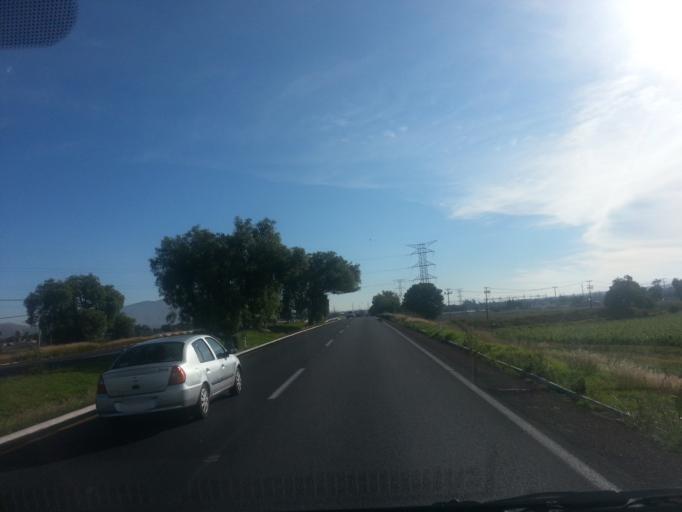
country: MX
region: Morelos
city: Xometla
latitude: 19.6418
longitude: -98.8965
